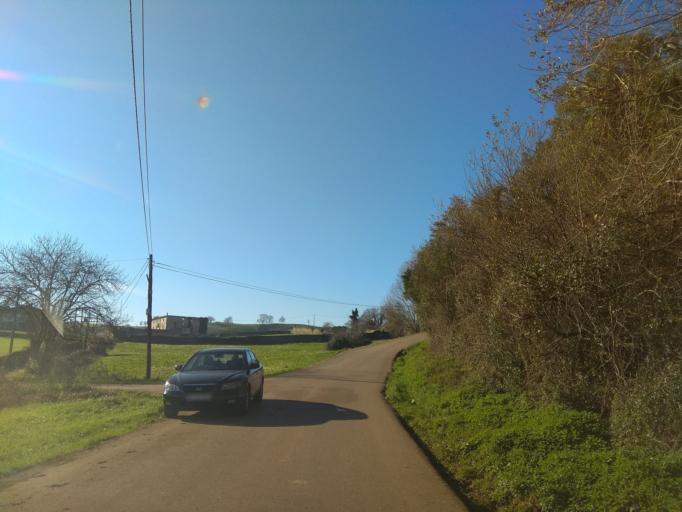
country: ES
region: Cantabria
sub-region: Provincia de Cantabria
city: Entrambasaguas
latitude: 43.3775
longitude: -3.6917
